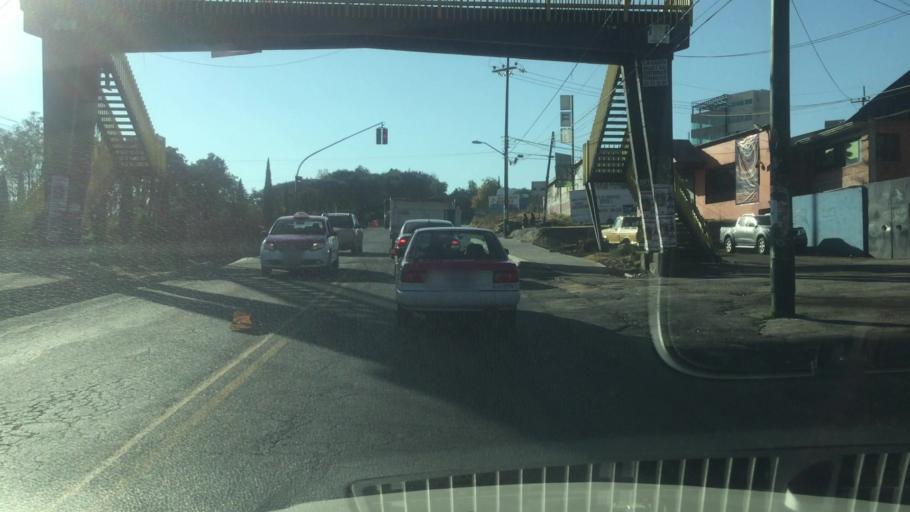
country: MX
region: Mexico City
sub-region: Tlalpan
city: Lomas de Tepemecatl
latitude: 19.2680
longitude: -99.2051
